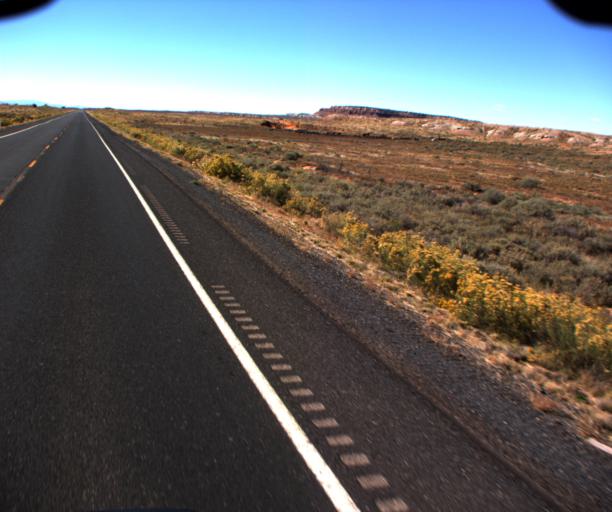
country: US
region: Arizona
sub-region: Coconino County
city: Fredonia
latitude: 36.9396
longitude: -112.5491
